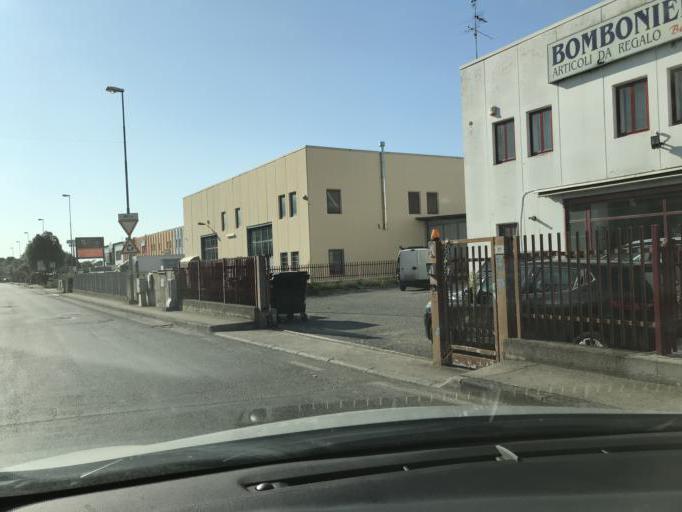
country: IT
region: Umbria
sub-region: Provincia di Perugia
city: Chiugiana-La Commenda
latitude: 43.1008
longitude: 12.3171
